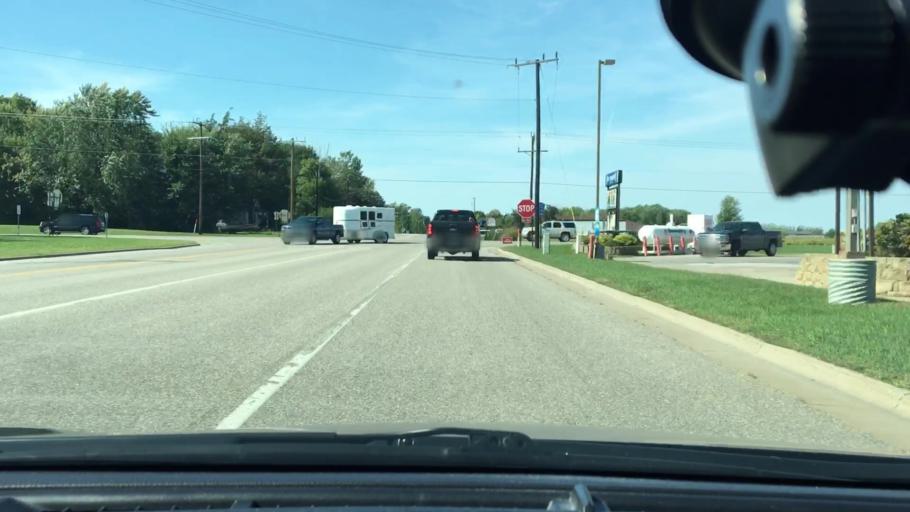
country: US
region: Minnesota
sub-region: Wright County
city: Hanover
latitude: 45.1237
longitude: -93.6349
